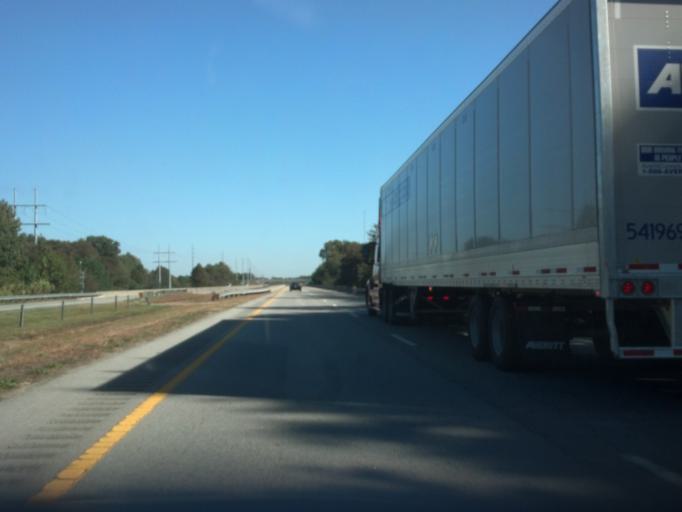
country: US
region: North Carolina
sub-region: Pitt County
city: Greenville
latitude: 35.6441
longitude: -77.4231
